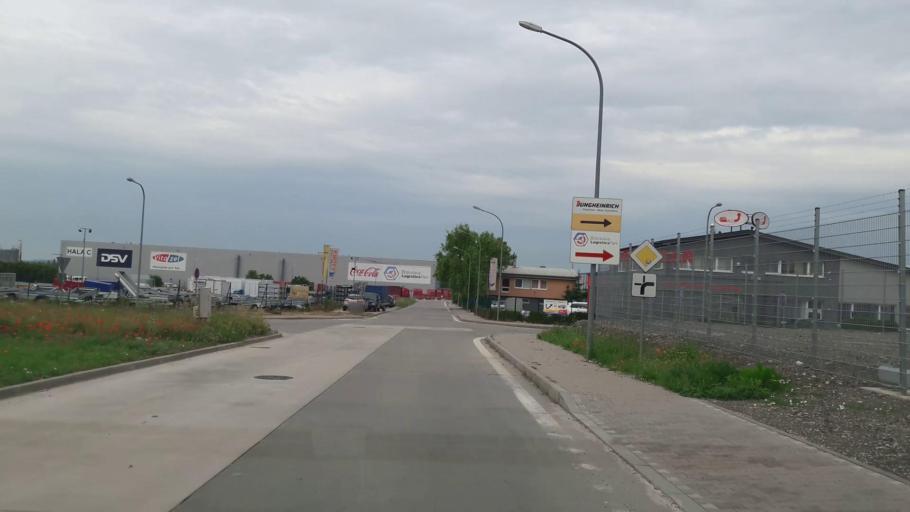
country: SK
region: Bratislavsky
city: Senec
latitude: 48.2301
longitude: 17.3727
